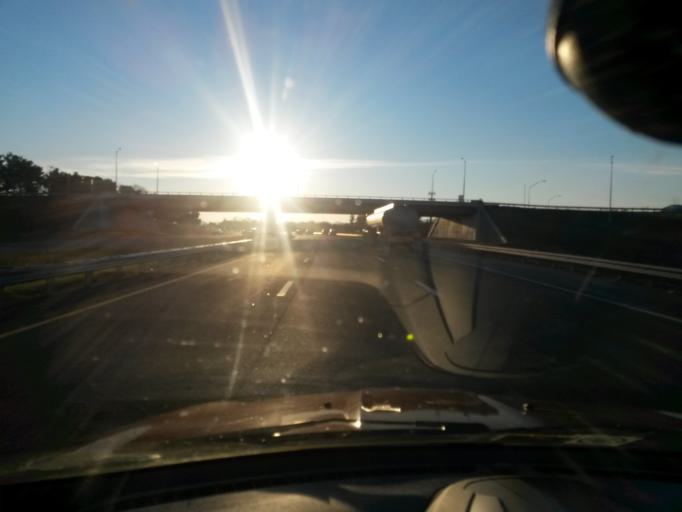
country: US
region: Virginia
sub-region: City of Roanoke
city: Roanoke
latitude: 37.2979
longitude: -79.9597
